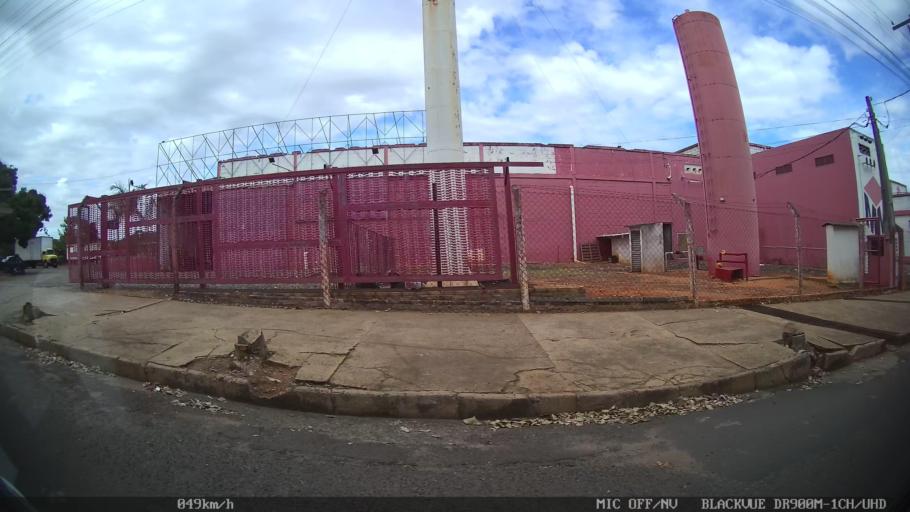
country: BR
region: Sao Paulo
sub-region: Sao Jose Do Rio Preto
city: Sao Jose do Rio Preto
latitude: -20.8101
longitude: -49.4981
